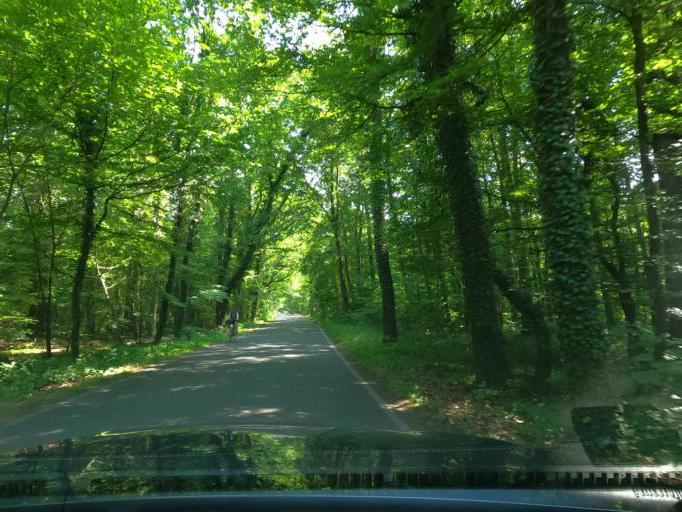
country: DE
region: Lower Saxony
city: Isernhagen Farster Bauerschaft
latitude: 52.4057
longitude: 9.8541
